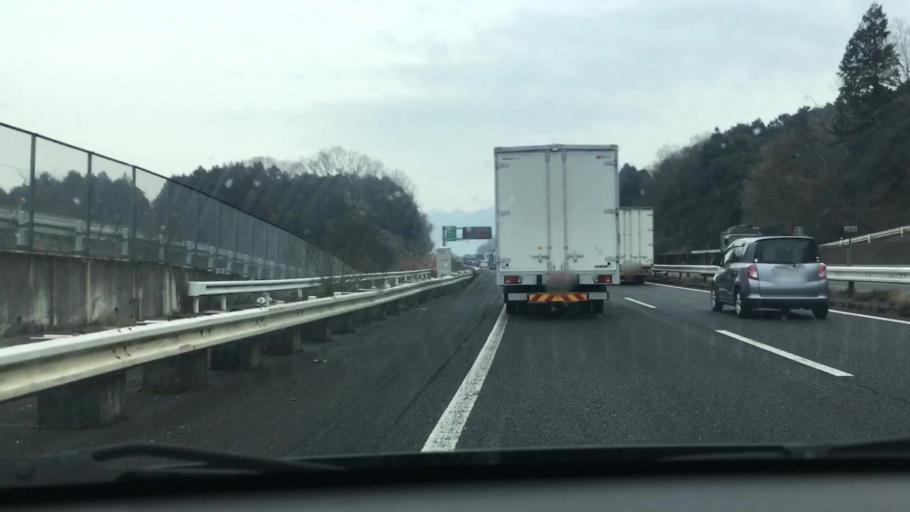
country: JP
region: Mie
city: Ueno-ebisumachi
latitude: 34.8240
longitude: 136.2279
